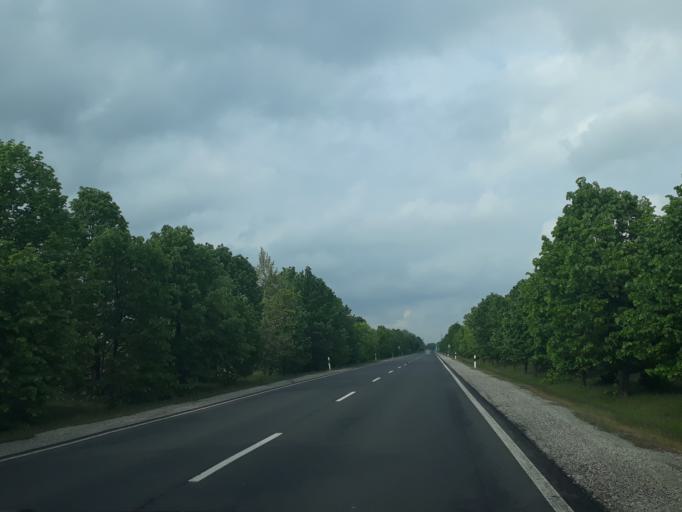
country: HU
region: Szabolcs-Szatmar-Bereg
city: Ajak
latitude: 48.1992
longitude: 22.0466
